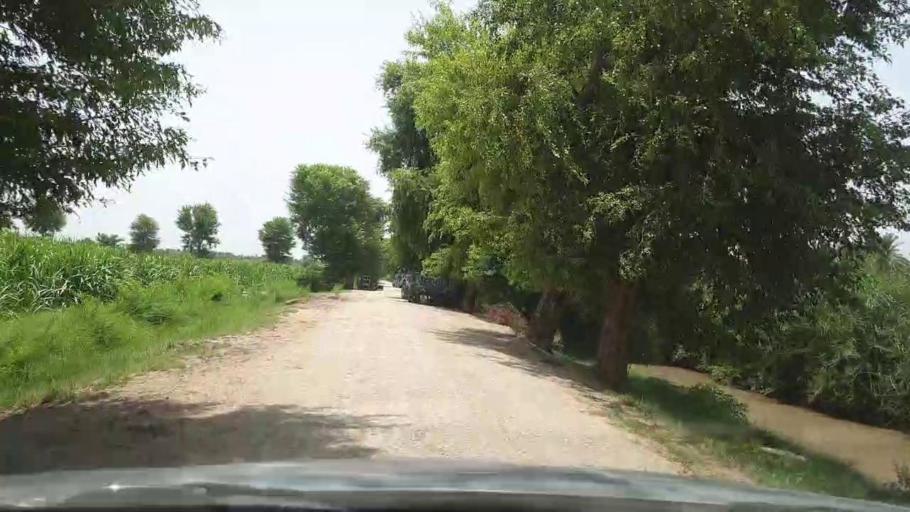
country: PK
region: Sindh
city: Pano Aqil
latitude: 27.8586
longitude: 69.0879
